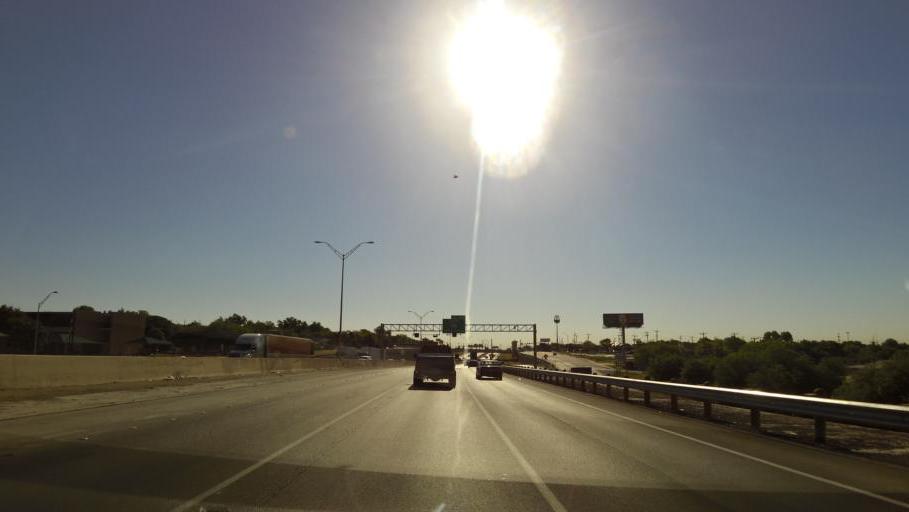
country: US
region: Texas
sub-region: Bexar County
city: Terrell Hills
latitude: 29.4389
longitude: -98.4545
